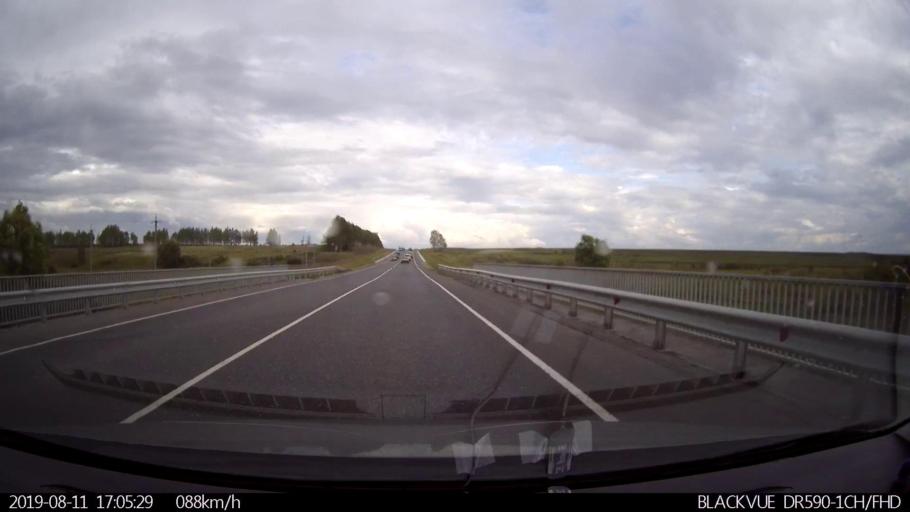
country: RU
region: Ulyanovsk
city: Mayna
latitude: 54.2982
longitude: 47.7871
